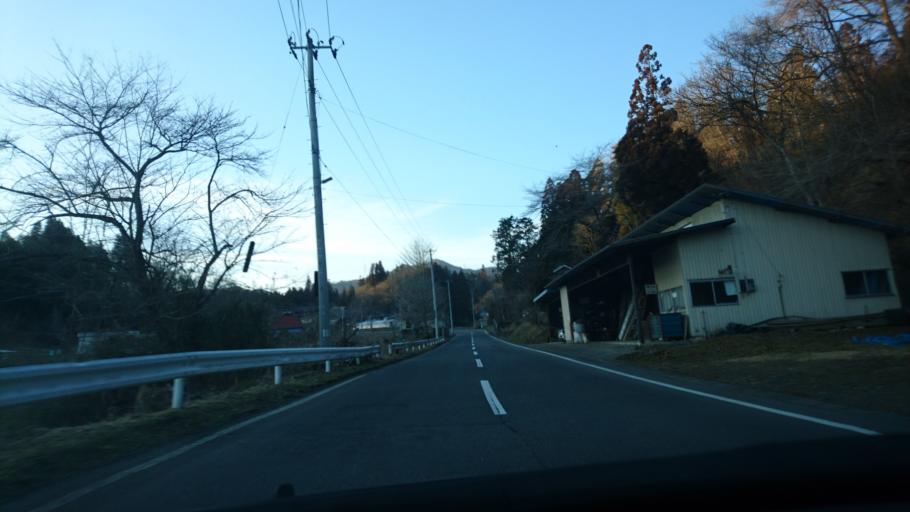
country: JP
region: Iwate
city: Mizusawa
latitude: 39.0425
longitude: 141.3405
